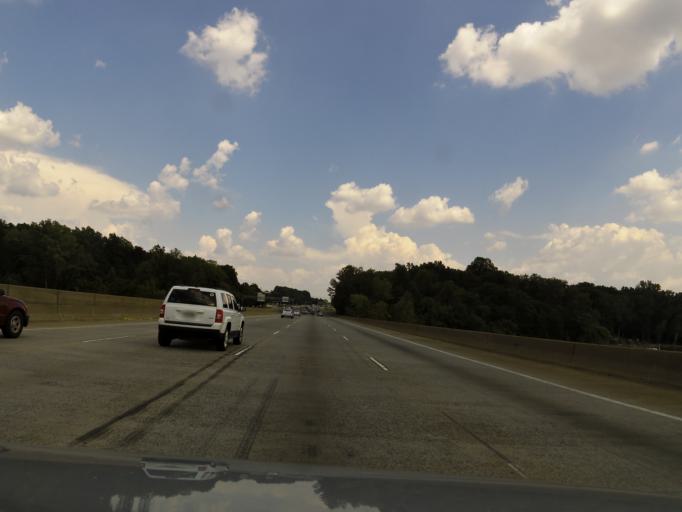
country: US
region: North Carolina
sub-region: Gaston County
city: Belmont
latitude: 35.2576
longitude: -81.0145
